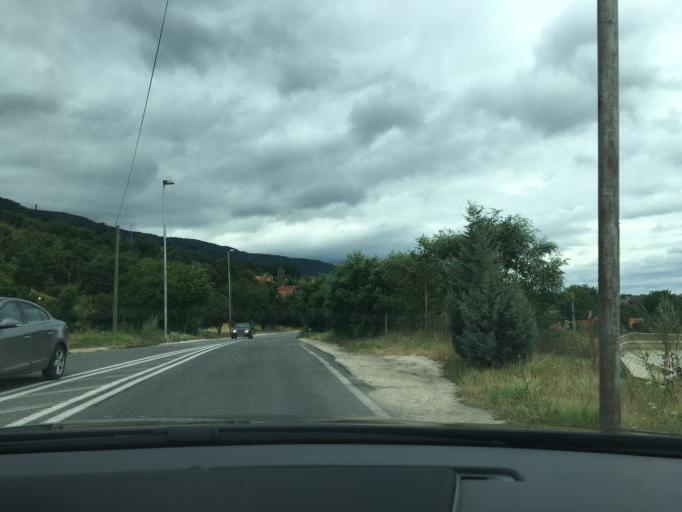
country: MK
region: Kriva Palanka
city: Kriva Palanka
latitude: 42.1918
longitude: 22.3089
